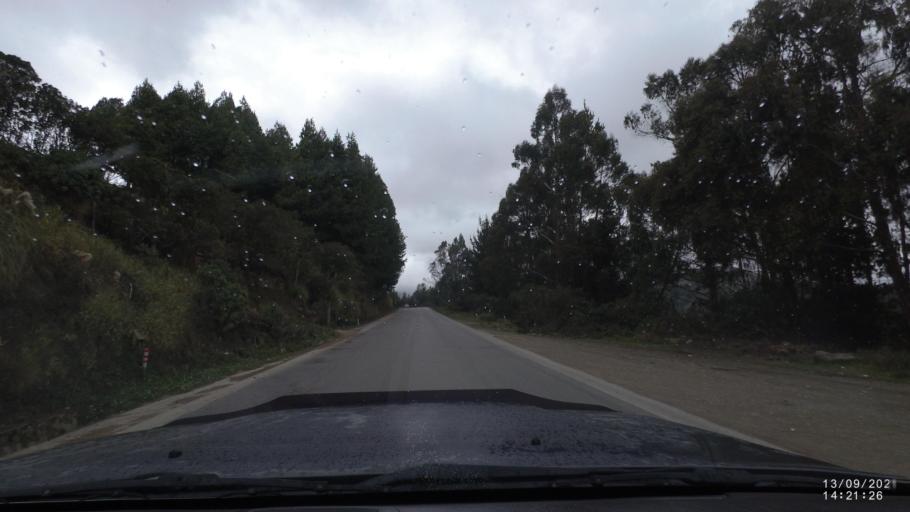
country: BO
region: Cochabamba
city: Colomi
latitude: -17.2593
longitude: -65.8898
